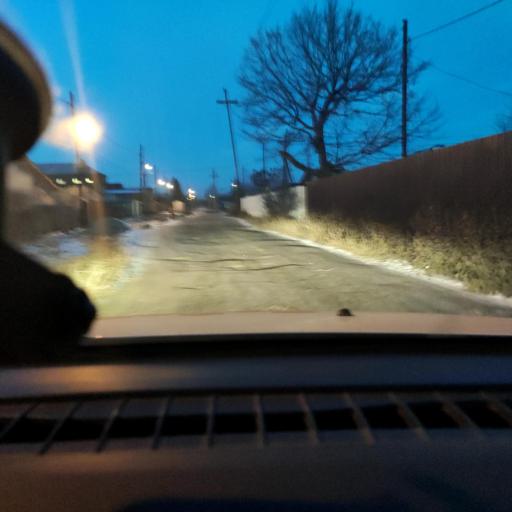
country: RU
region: Samara
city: Smyshlyayevka
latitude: 53.2533
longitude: 50.3551
